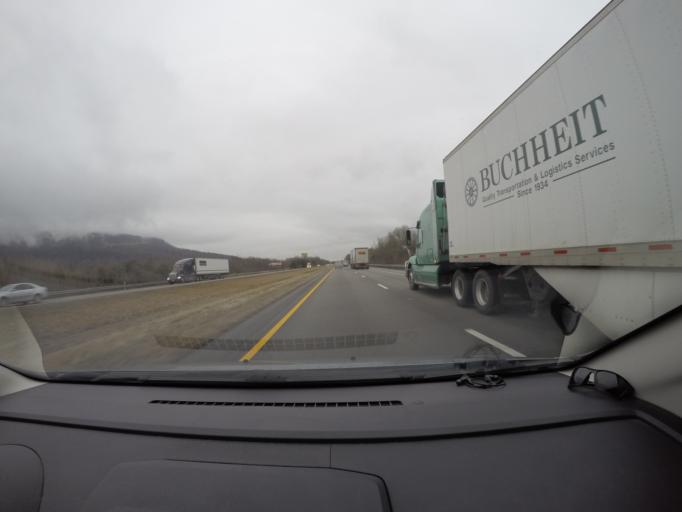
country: US
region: Tennessee
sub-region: Marion County
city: South Pittsburg
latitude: 35.0542
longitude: -85.7152
